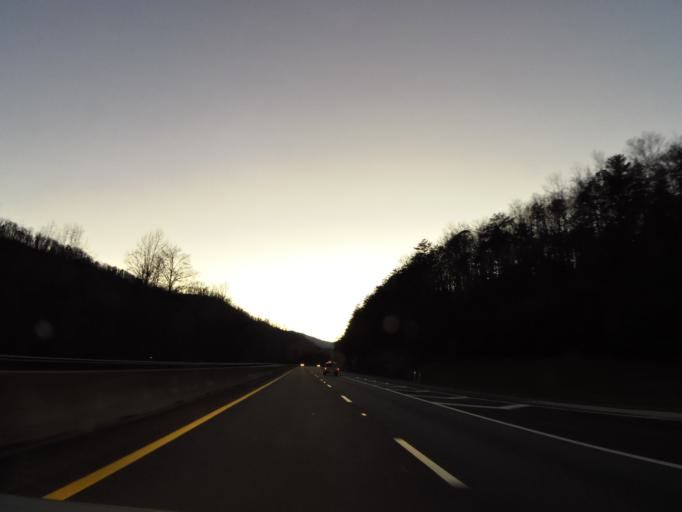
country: US
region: Tennessee
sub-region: Cocke County
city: Newport
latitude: 35.8174
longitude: -83.1603
